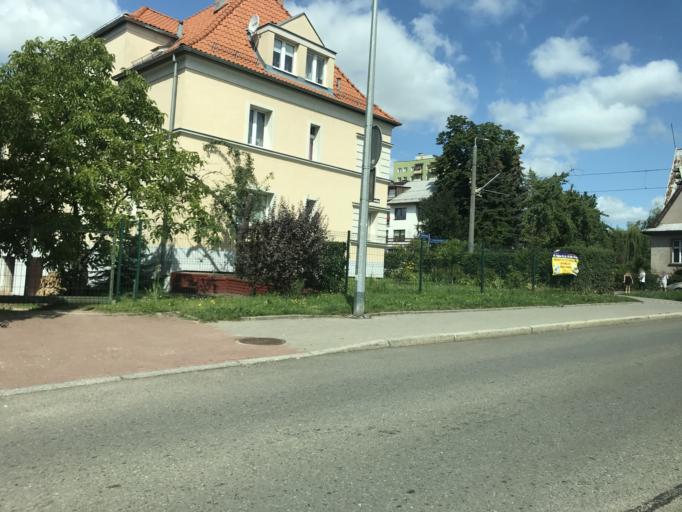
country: PL
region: Warmian-Masurian Voivodeship
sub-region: Powiat elblaski
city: Elblag
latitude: 54.1586
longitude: 19.4214
